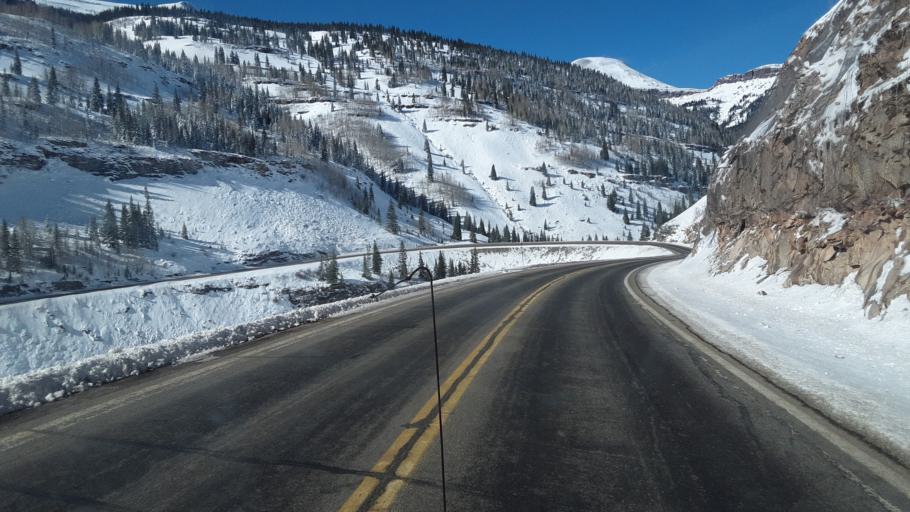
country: US
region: Colorado
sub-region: San Juan County
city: Silverton
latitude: 37.7288
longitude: -107.7480
